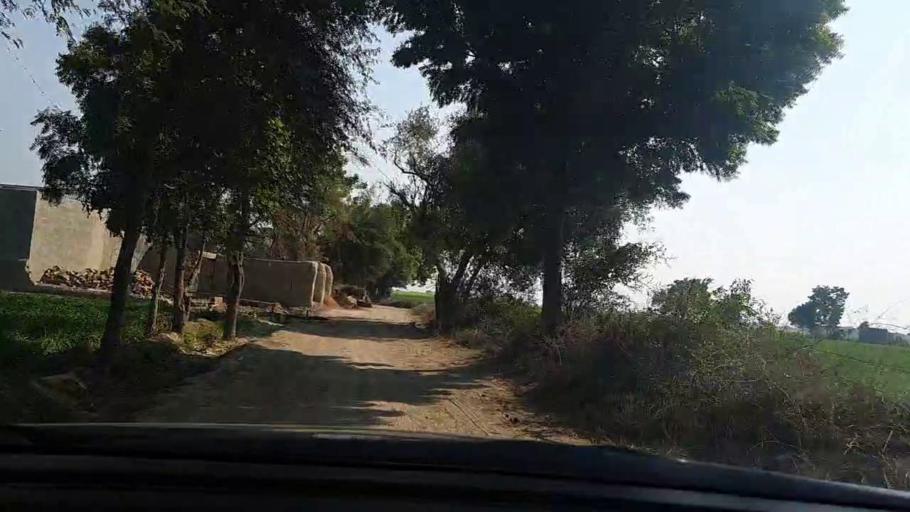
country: PK
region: Sindh
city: Sann
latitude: 26.2656
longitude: 68.0725
